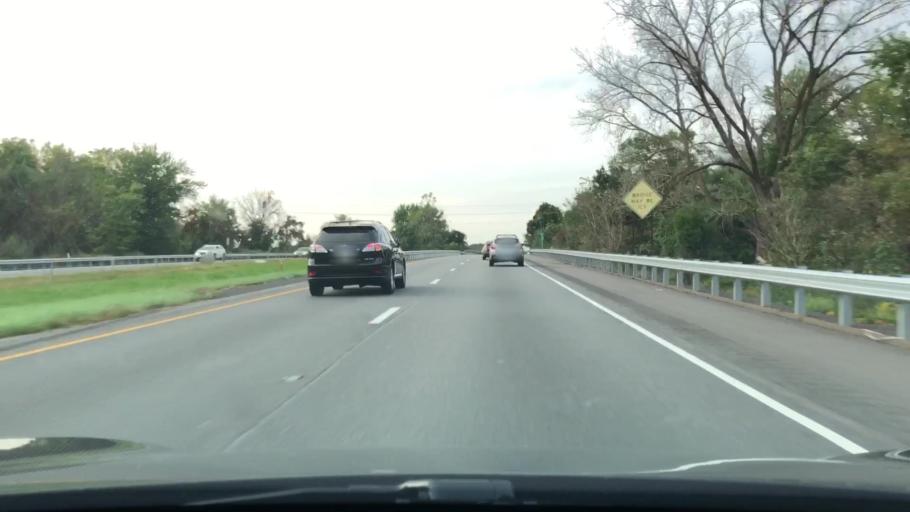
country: US
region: Pennsylvania
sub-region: Bucks County
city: Woodside
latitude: 40.2183
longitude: -74.8791
